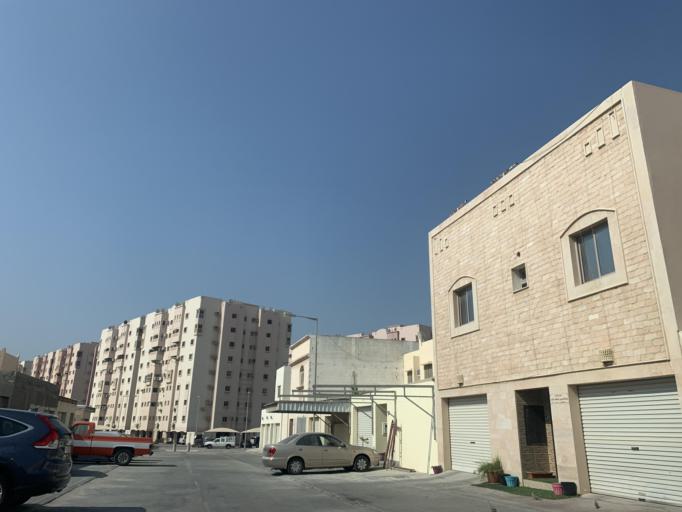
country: BH
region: Central Governorate
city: Madinat Hamad
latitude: 26.1213
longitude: 50.4905
